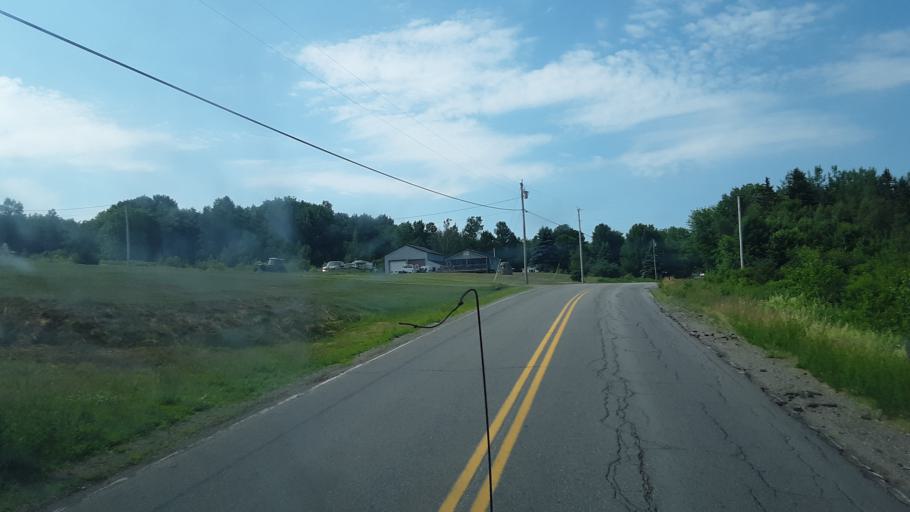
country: US
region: Maine
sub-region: Waldo County
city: Frankfort
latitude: 44.5884
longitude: -68.9443
